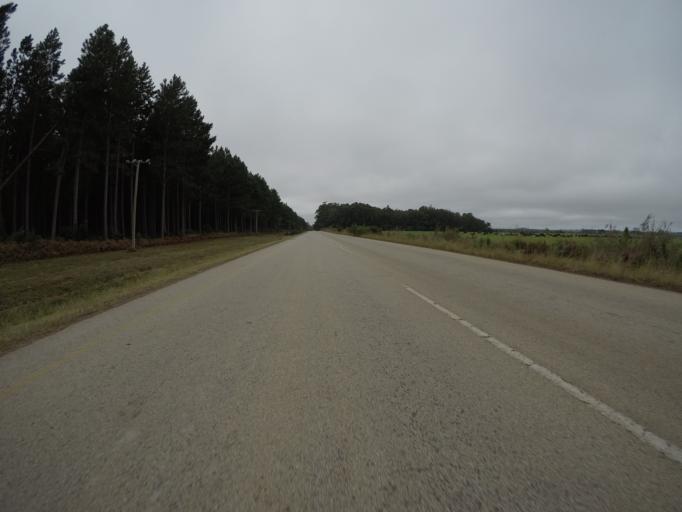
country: ZA
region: Eastern Cape
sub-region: Cacadu District Municipality
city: Kareedouw
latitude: -33.9941
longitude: 24.1055
